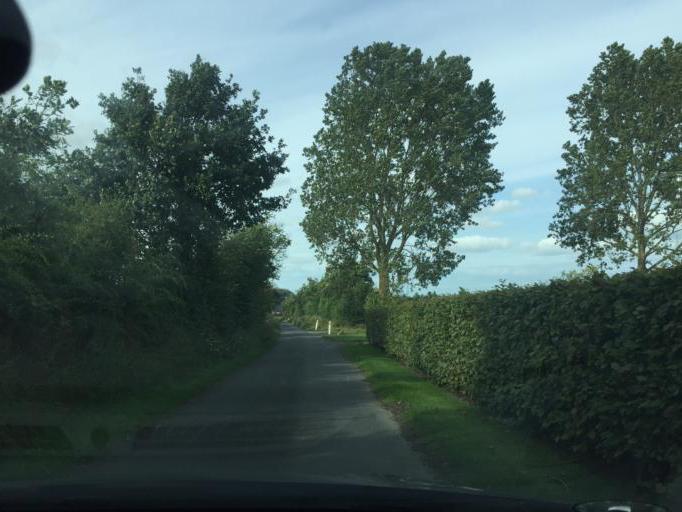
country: DK
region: South Denmark
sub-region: Faaborg-Midtfyn Kommune
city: Arslev
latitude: 55.3469
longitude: 10.5132
